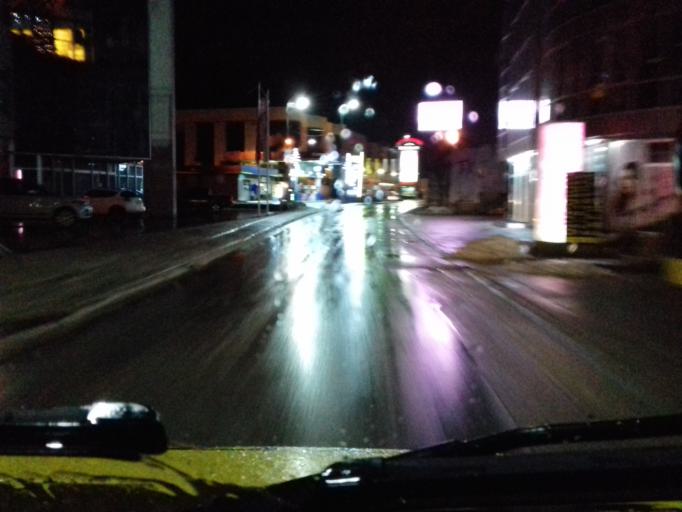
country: BA
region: Federation of Bosnia and Herzegovina
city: Kiseljak
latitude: 43.9407
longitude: 18.0793
